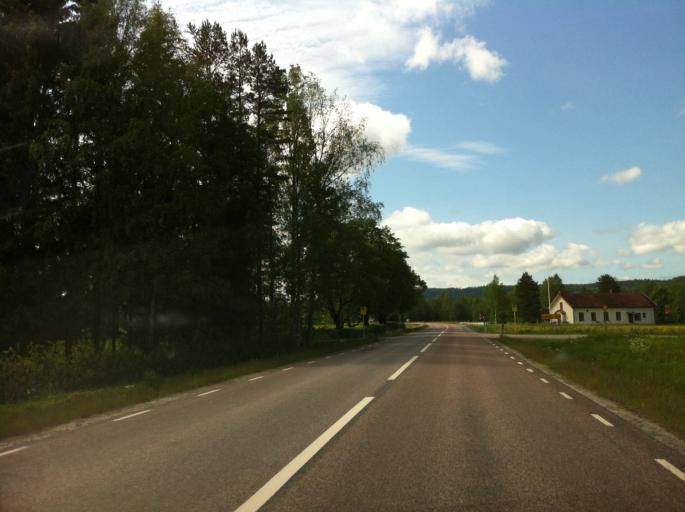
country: SE
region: Vaermland
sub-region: Sunne Kommun
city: Sunne
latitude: 59.6912
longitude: 13.1406
